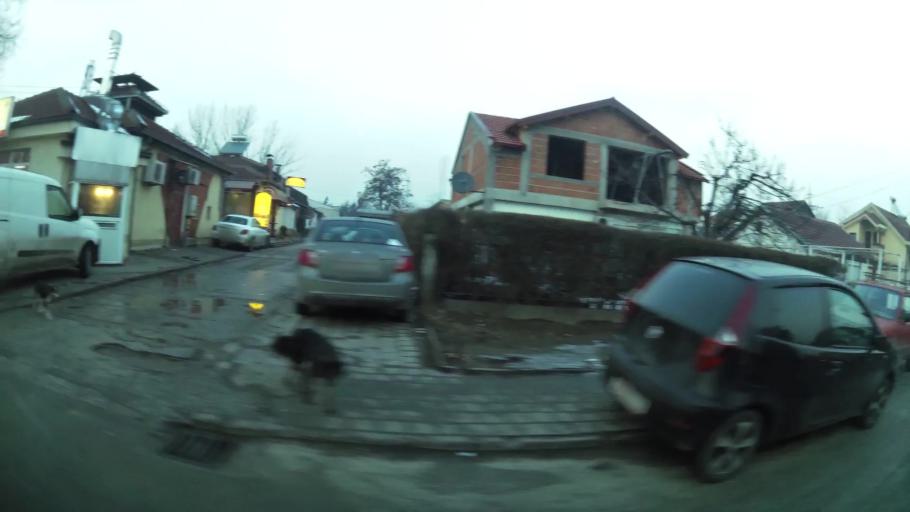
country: MK
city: Creshevo
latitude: 42.0042
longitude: 21.5050
